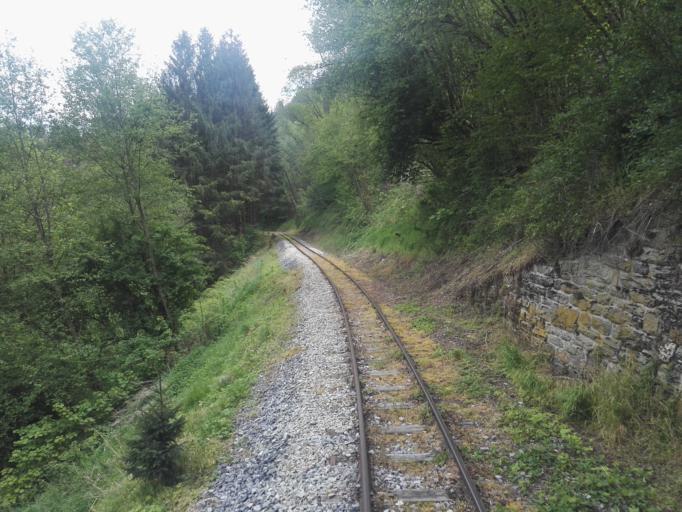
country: AT
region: Styria
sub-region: Politischer Bezirk Weiz
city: Birkfeld
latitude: 47.3487
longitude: 15.6974
